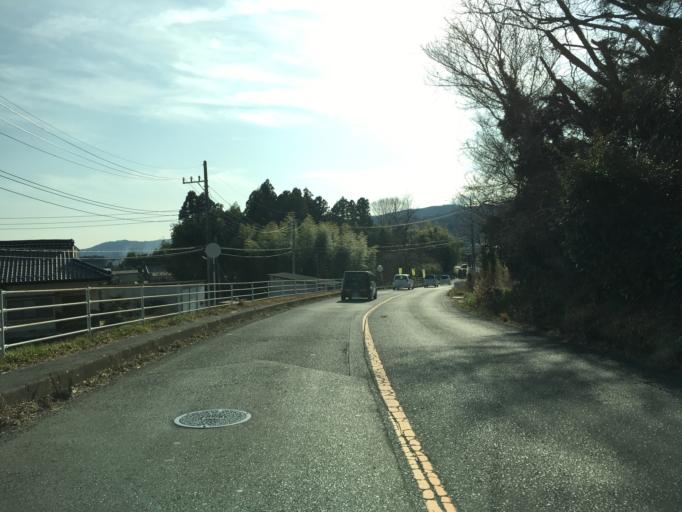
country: JP
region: Ibaraki
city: Takahagi
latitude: 36.7246
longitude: 140.6822
